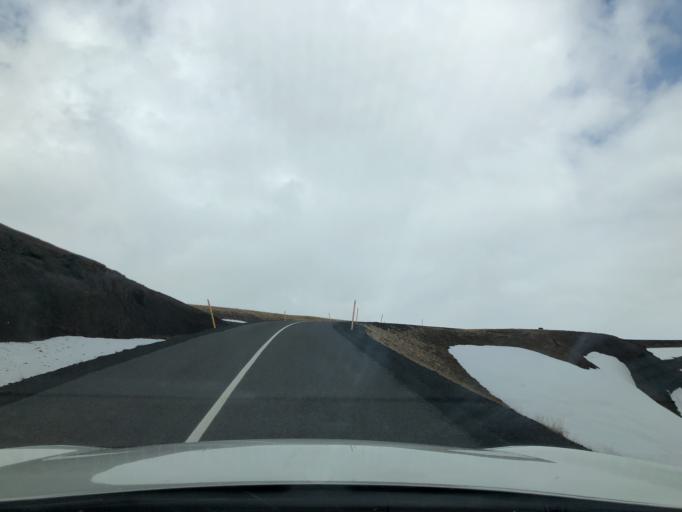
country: IS
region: Northeast
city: Laugar
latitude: 65.7105
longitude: -16.7733
